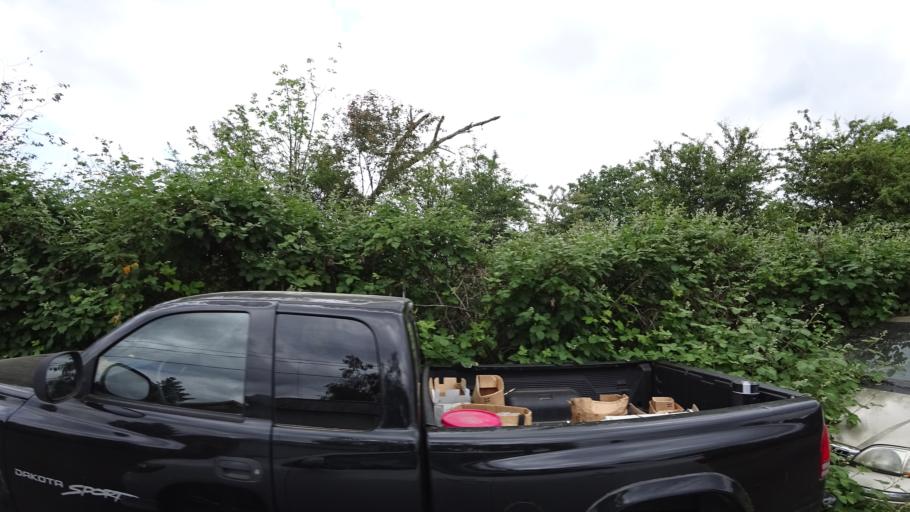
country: US
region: Oregon
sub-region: Multnomah County
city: Lents
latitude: 45.5066
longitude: -122.5539
